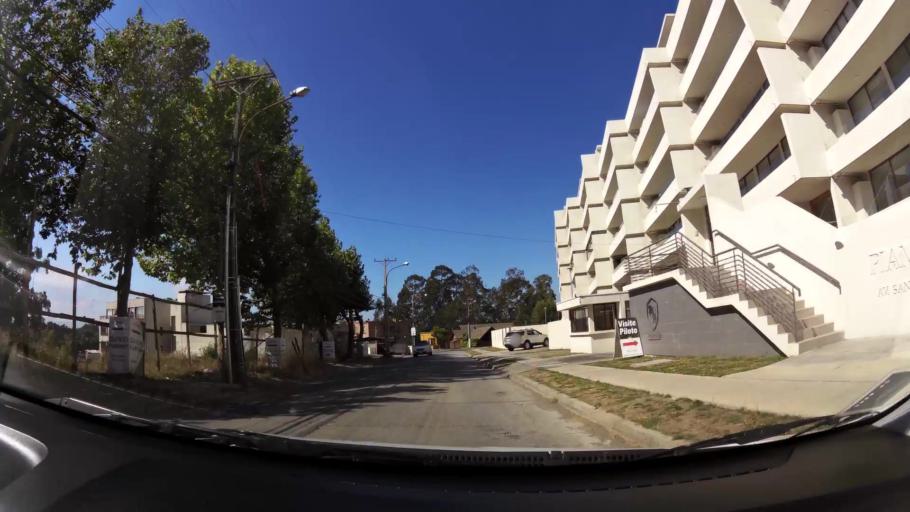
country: CL
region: Biobio
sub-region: Provincia de Concepcion
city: Concepcion
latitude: -36.7918
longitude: -73.0601
